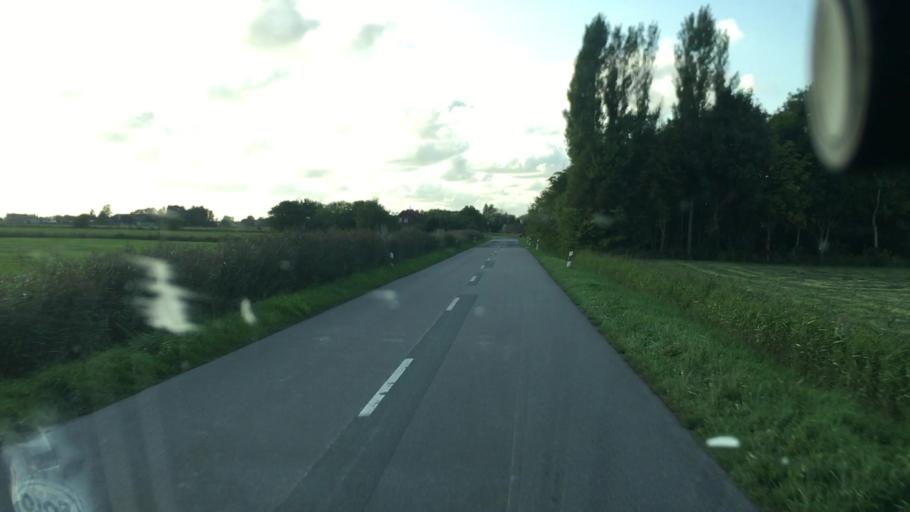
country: DE
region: Lower Saxony
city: Werdum
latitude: 53.6788
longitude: 7.7139
